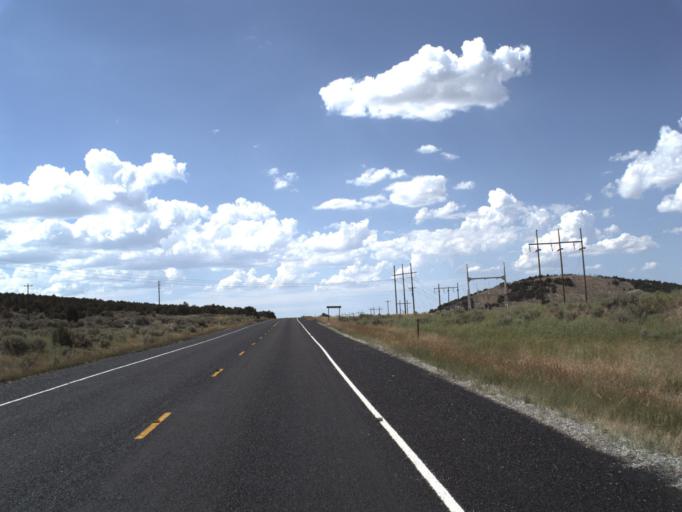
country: US
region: Idaho
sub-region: Minidoka County
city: Rupert
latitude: 41.9732
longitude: -113.1546
